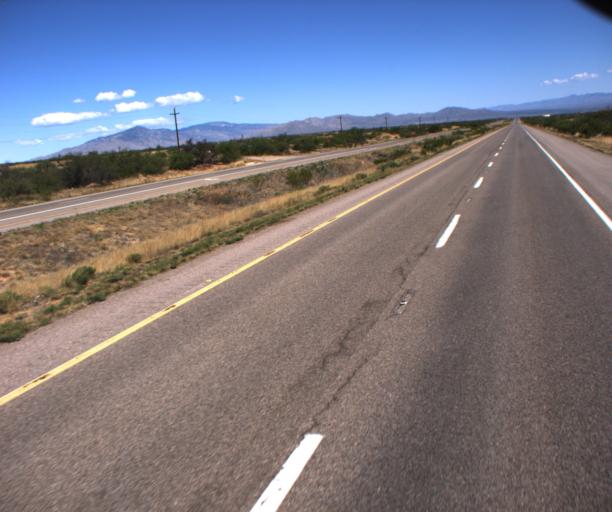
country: US
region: Arizona
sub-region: Cochise County
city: Whetstone
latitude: 31.8921
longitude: -110.3410
